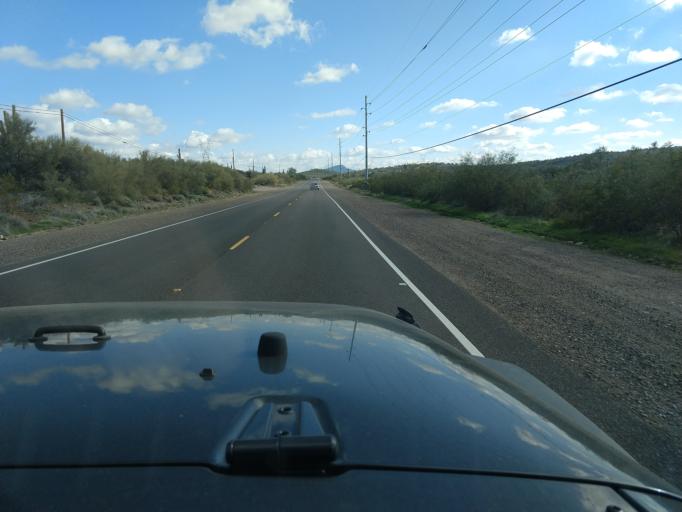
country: US
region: Arizona
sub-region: Maricopa County
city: New River
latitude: 33.9213
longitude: -112.1067
